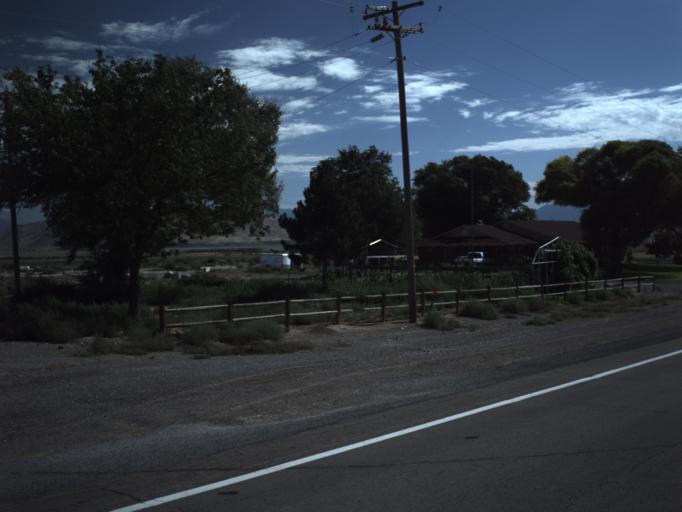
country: US
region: Utah
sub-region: Utah County
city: Genola
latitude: 39.9520
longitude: -111.9529
